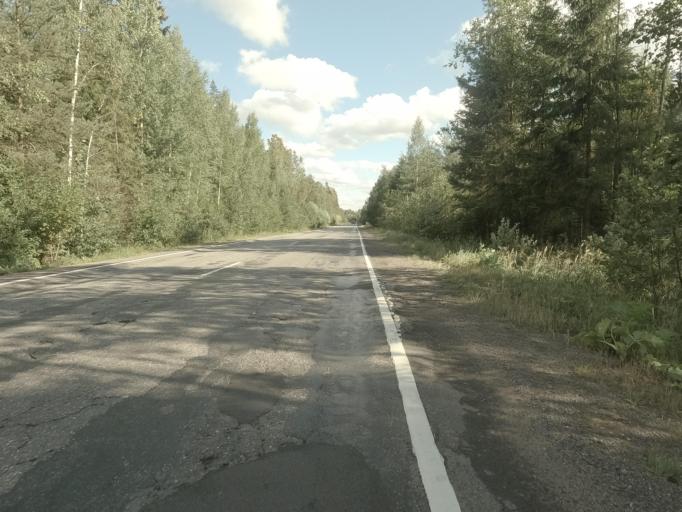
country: RU
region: Leningrad
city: Shcheglovo
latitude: 59.9913
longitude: 30.8827
